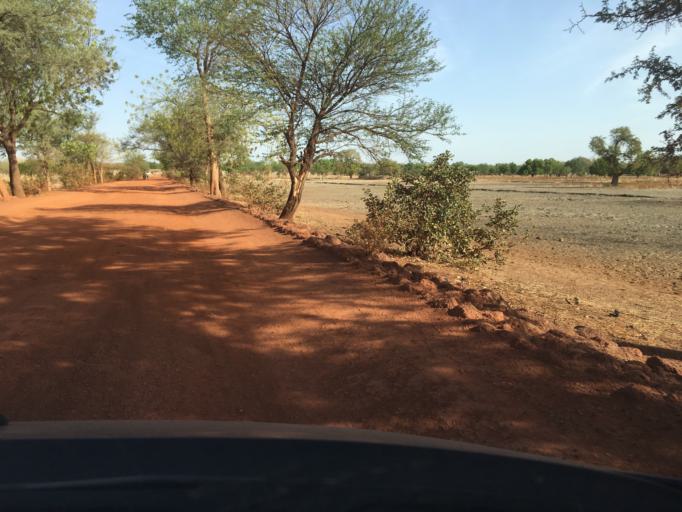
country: BF
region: Plateau-Central
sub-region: Province du Kourweogo
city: Bousse
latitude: 12.5708
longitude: -1.9280
